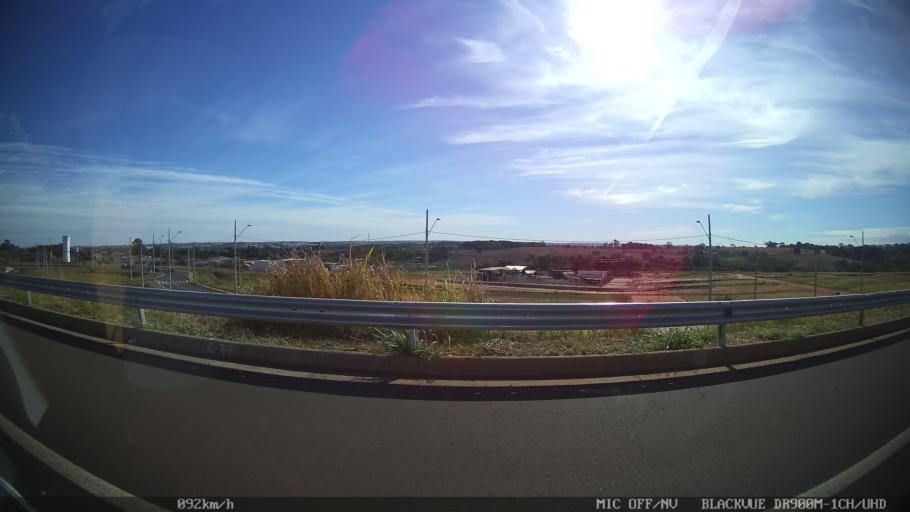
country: BR
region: Sao Paulo
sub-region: Sao Jose Do Rio Preto
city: Sao Jose do Rio Preto
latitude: -20.7594
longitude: -49.3454
